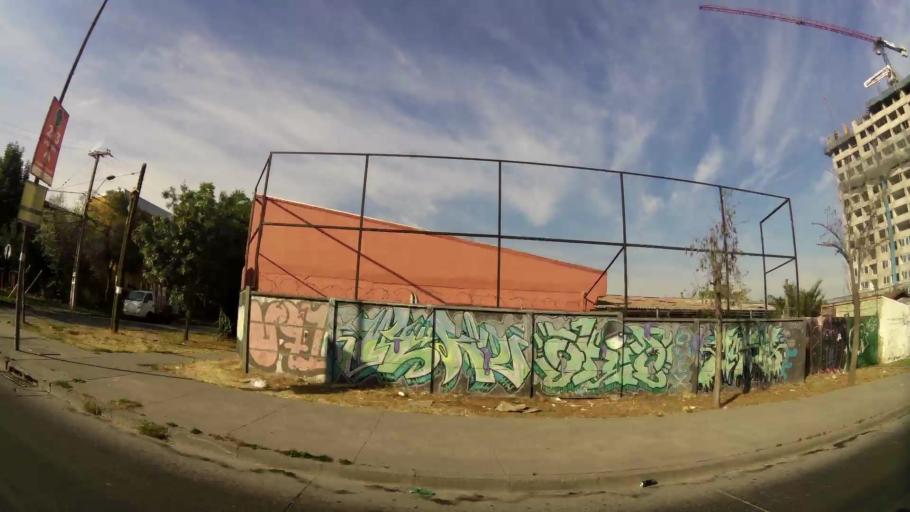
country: CL
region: Santiago Metropolitan
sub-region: Provincia de Santiago
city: Santiago
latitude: -33.5046
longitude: -70.6506
